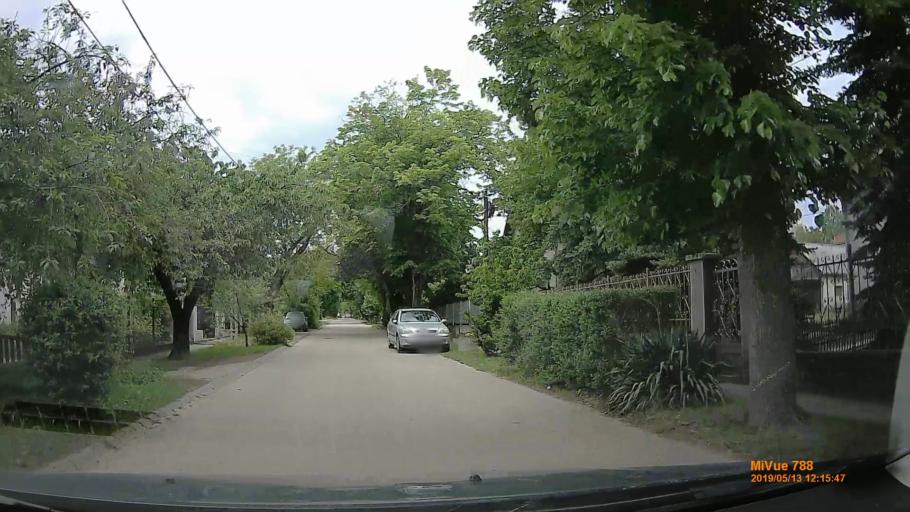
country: HU
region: Pest
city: Diosd
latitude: 47.4020
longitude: 18.9856
